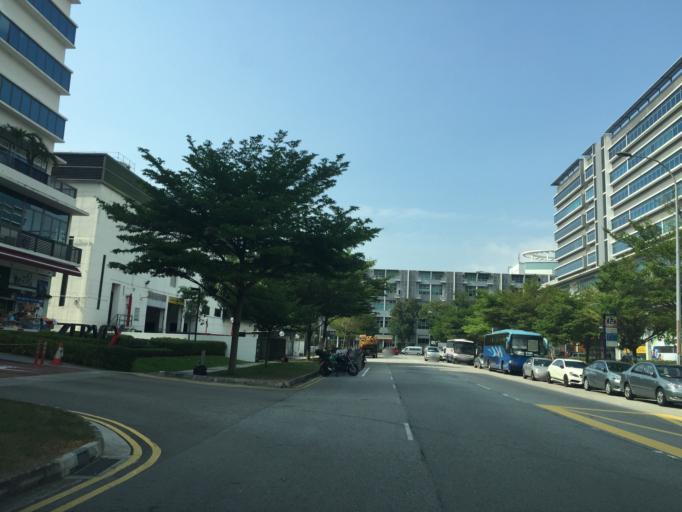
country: SG
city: Singapore
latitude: 1.3338
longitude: 103.8949
